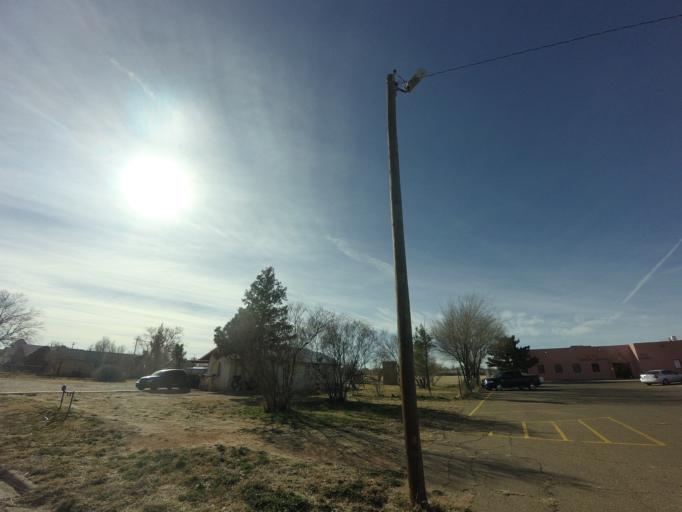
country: US
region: New Mexico
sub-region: Curry County
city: Clovis
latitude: 34.4097
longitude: -103.2230
